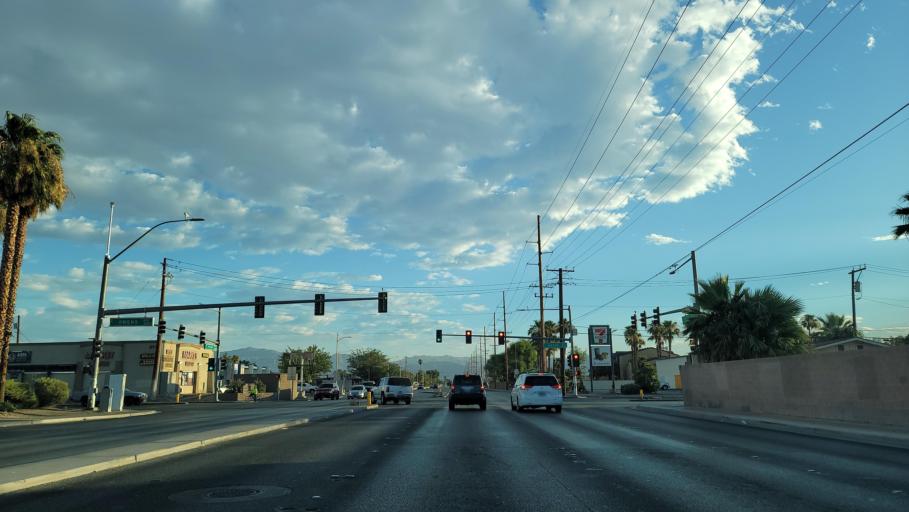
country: US
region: Nevada
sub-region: Clark County
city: North Las Vegas
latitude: 36.1876
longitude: -115.0983
